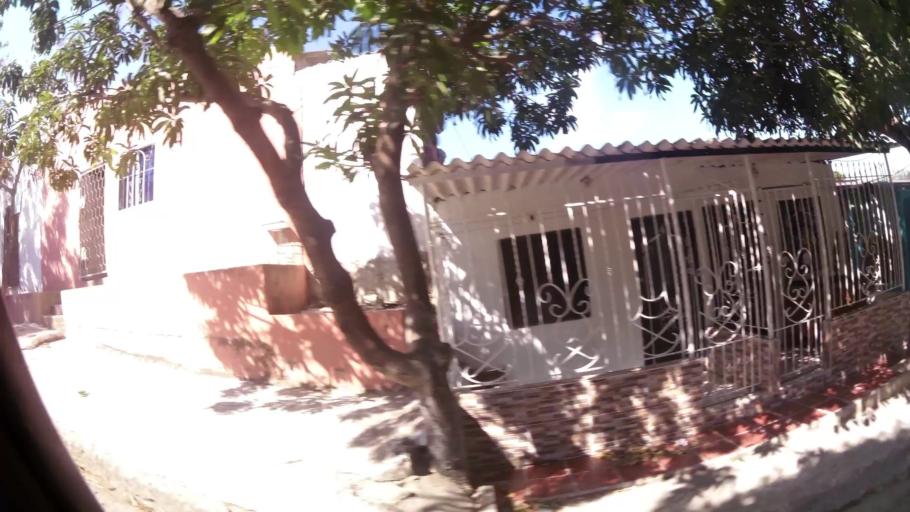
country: CO
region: Atlantico
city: Barranquilla
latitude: 10.9324
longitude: -74.8302
